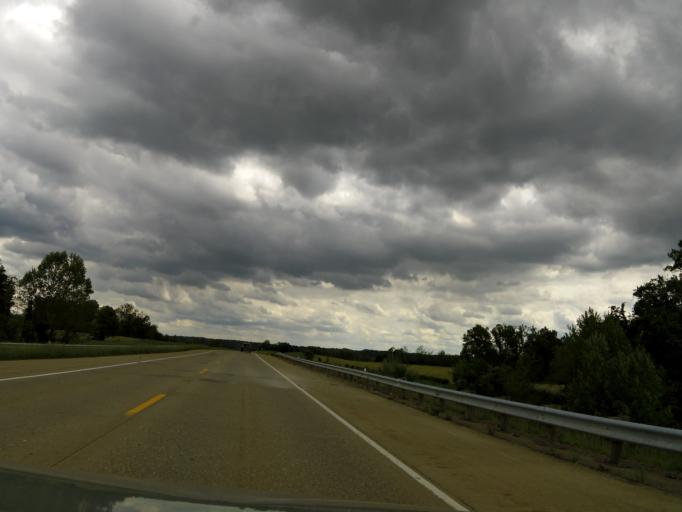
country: US
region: West Virginia
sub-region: Jackson County
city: Ravenswood
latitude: 38.9418
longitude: -81.7917
